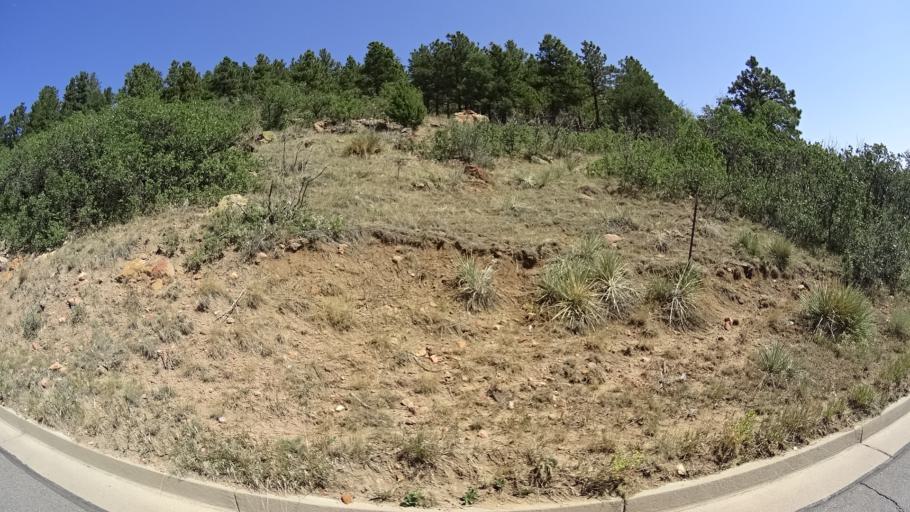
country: US
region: Colorado
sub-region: El Paso County
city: Air Force Academy
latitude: 38.9421
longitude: -104.8740
